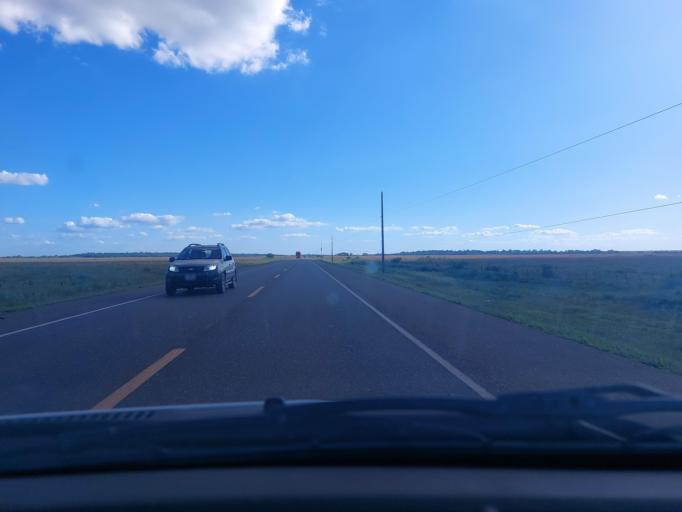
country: PY
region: San Pedro
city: Union
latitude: -24.8257
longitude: -56.7757
